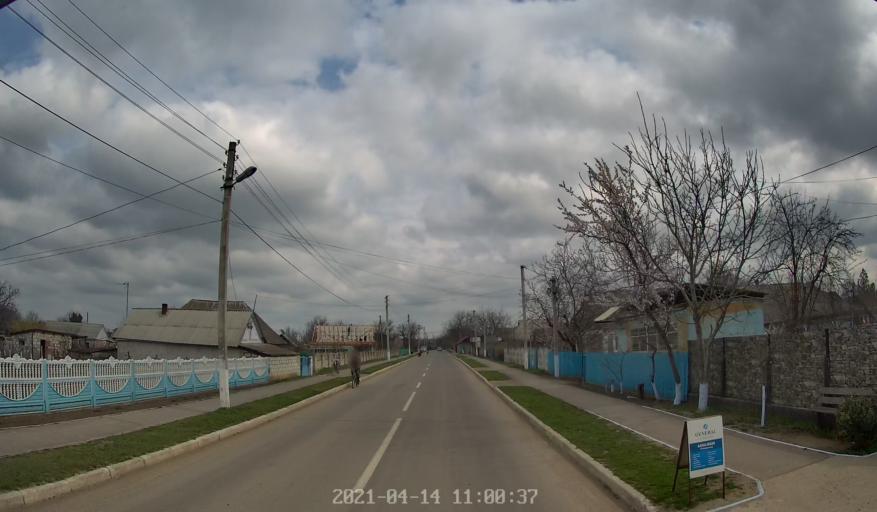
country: MD
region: Criuleni
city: Criuleni
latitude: 47.1496
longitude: 29.1399
